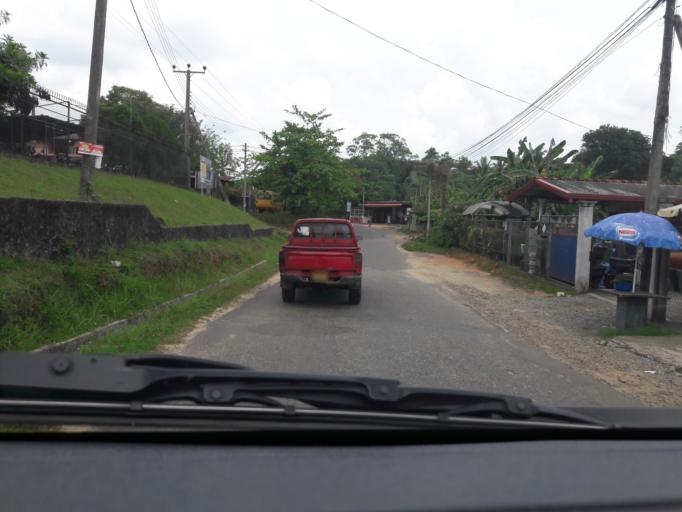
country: LK
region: Southern
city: Hikkaduwa
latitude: 6.2502
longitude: 80.2677
